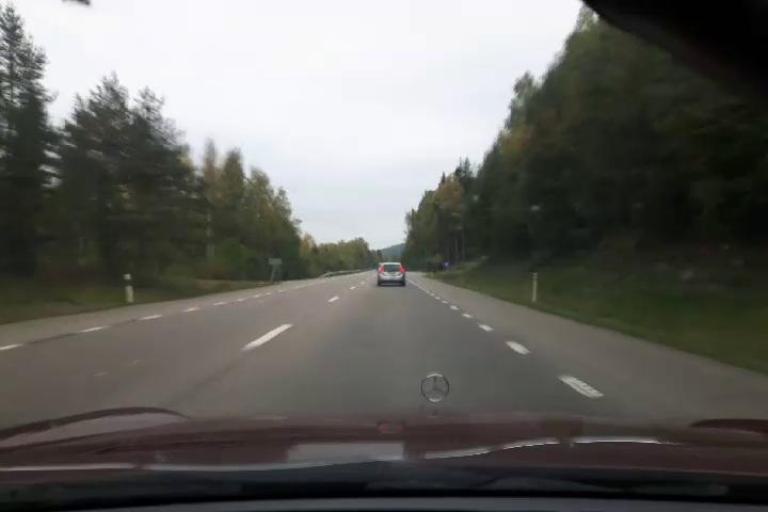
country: SE
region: Vaesternorrland
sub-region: Kramfors Kommun
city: Nordingra
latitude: 63.0374
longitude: 18.3266
